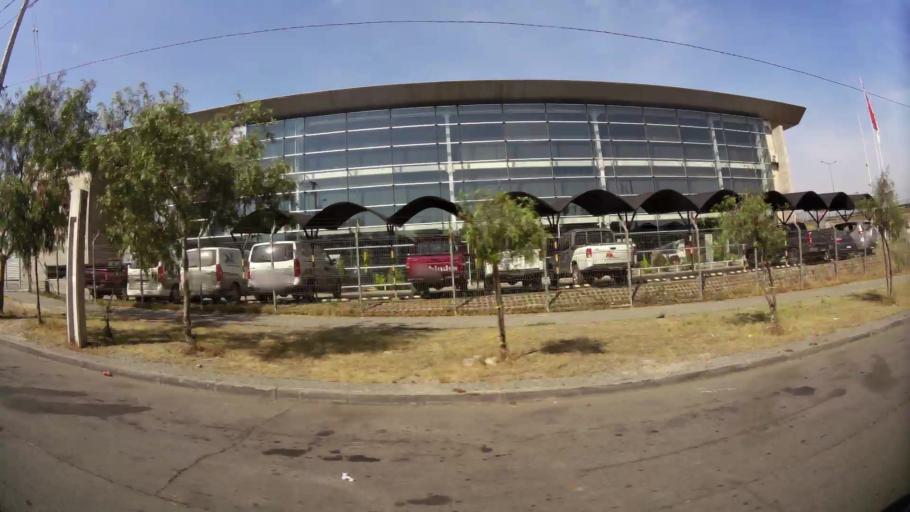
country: CL
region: Santiago Metropolitan
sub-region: Provincia de Santiago
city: Lo Prado
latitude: -33.4214
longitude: -70.7818
